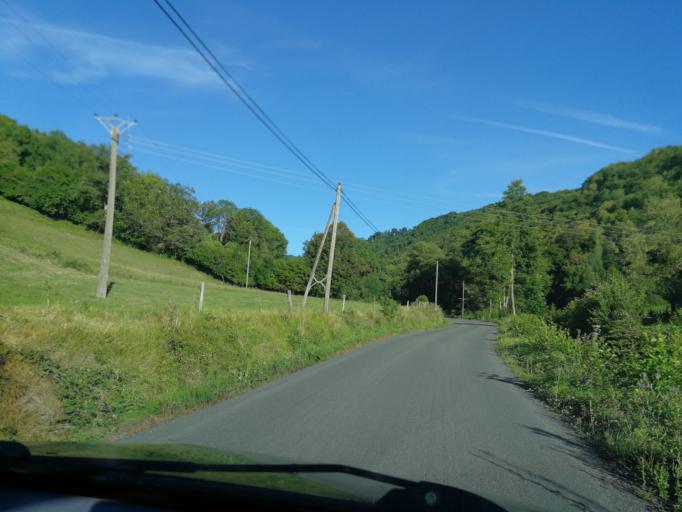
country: FR
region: Auvergne
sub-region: Departement du Cantal
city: Saint-Cernin
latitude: 45.1018
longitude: 2.5330
